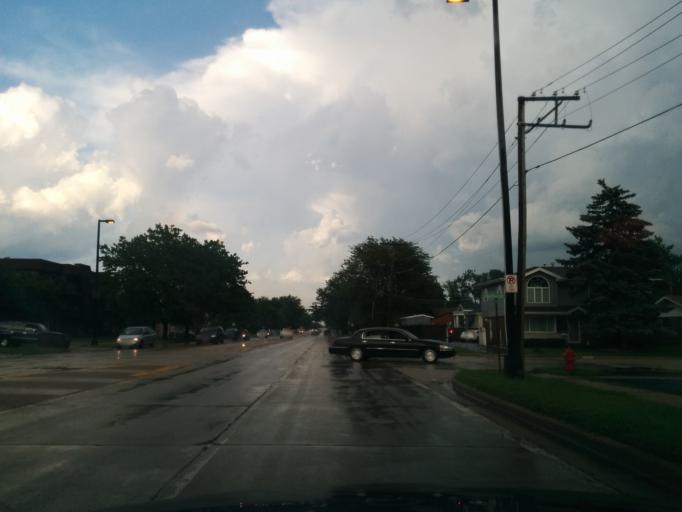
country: US
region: Illinois
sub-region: Cook County
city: Burbank
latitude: 41.7335
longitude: -87.7957
